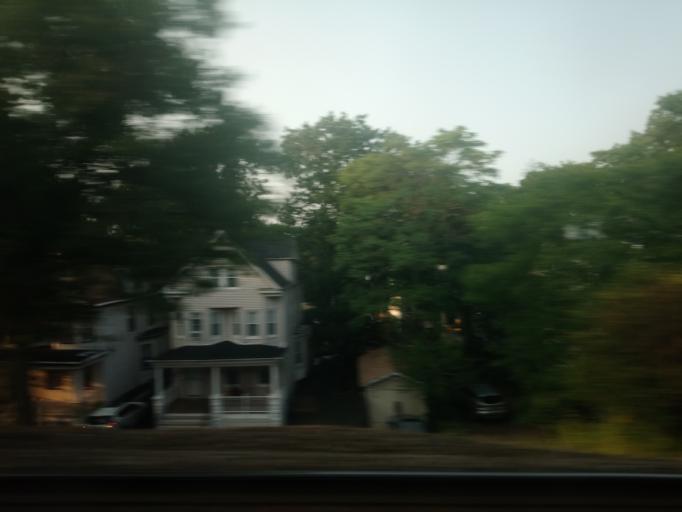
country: US
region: New Jersey
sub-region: Essex County
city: East Orange
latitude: 40.7598
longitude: -74.2068
